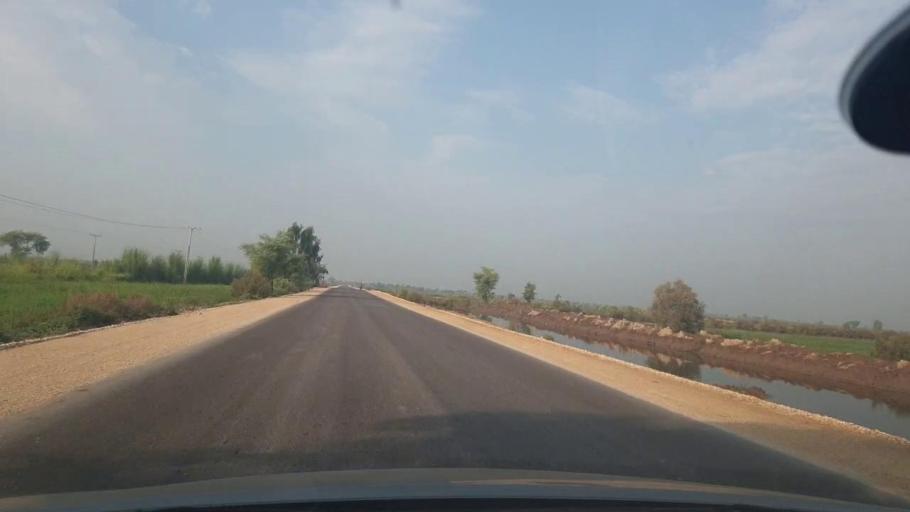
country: PK
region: Sindh
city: Jacobabad
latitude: 28.2270
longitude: 68.3800
